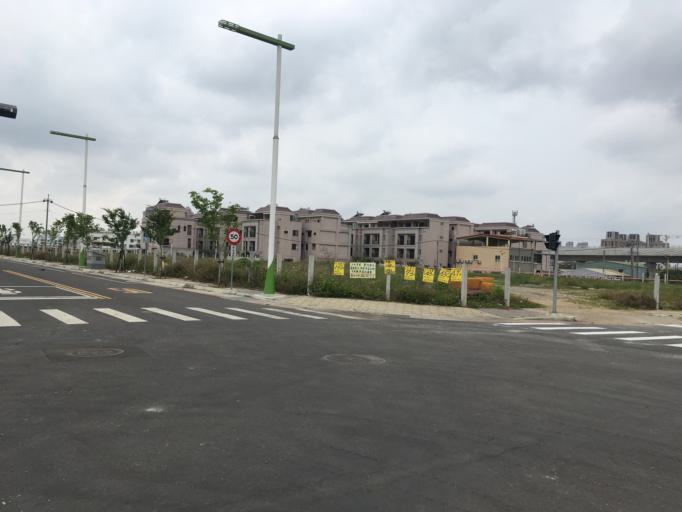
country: TW
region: Taiwan
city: Fengyuan
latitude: 24.1976
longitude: 120.7062
